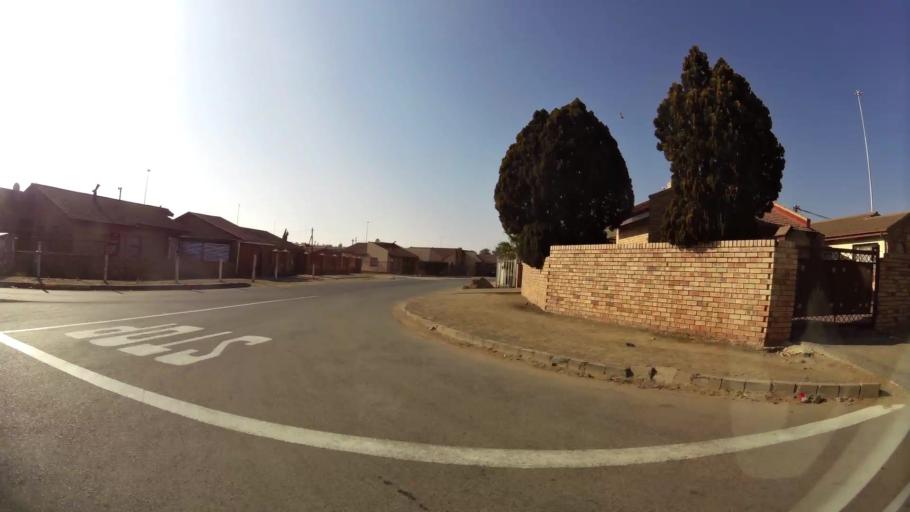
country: ZA
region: Orange Free State
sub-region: Mangaung Metropolitan Municipality
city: Bloemfontein
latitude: -29.1837
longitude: 26.2232
